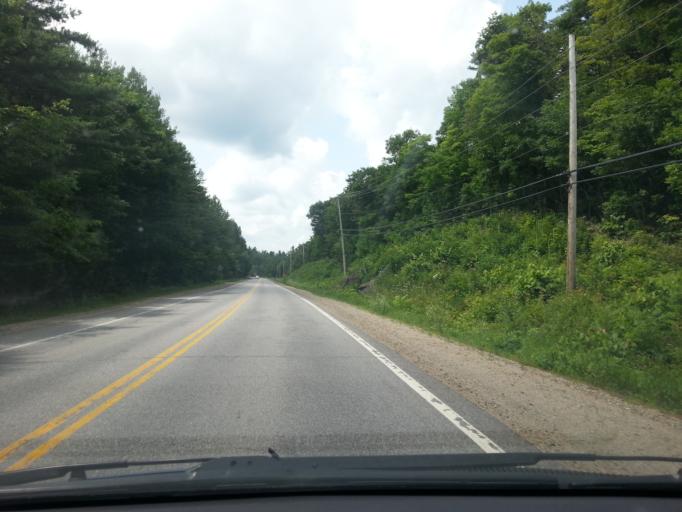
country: CA
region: Quebec
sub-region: Outaouais
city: Wakefield
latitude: 45.6365
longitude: -75.7969
